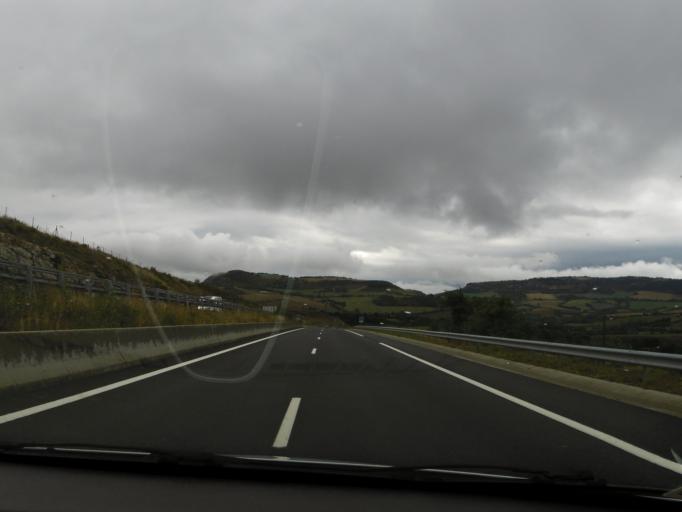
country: FR
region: Languedoc-Roussillon
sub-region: Departement de la Lozere
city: Chirac
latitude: 44.5010
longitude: 3.2580
